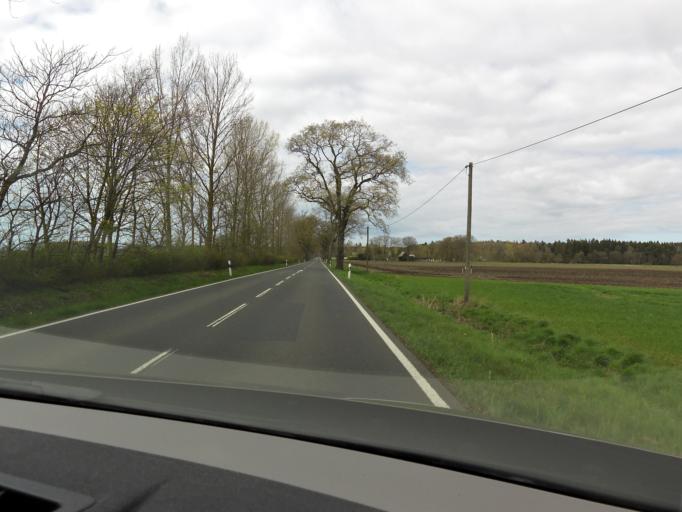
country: DE
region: Mecklenburg-Vorpommern
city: Gingst
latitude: 54.4129
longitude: 13.2864
